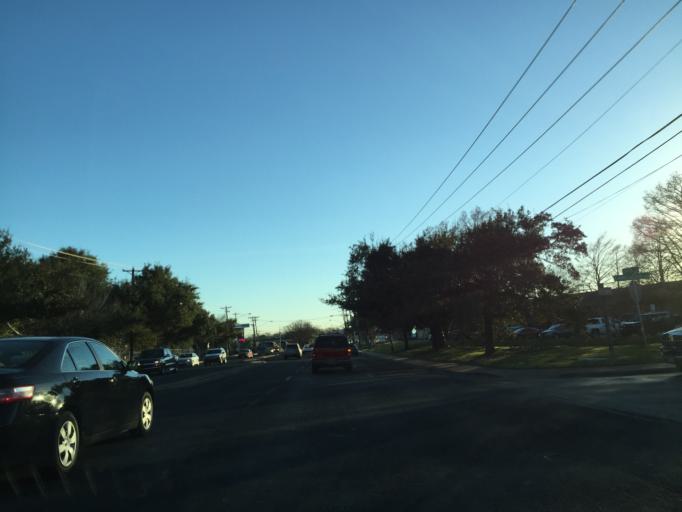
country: US
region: Texas
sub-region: Travis County
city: Austin
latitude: 30.3242
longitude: -97.6935
